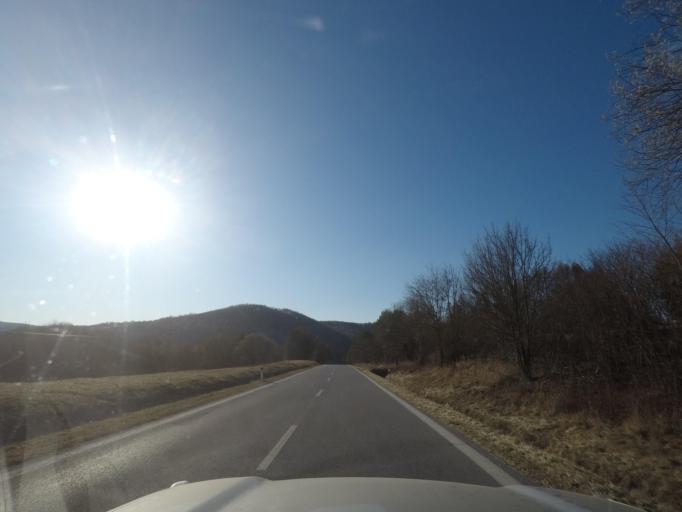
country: SK
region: Presovsky
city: Medzilaborce
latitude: 49.2523
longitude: 21.9183
